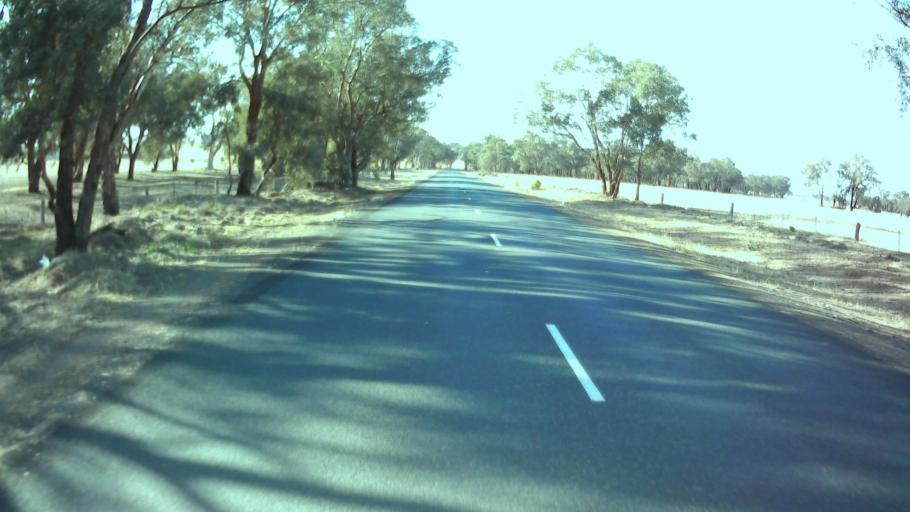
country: AU
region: New South Wales
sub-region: Weddin
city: Grenfell
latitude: -33.9466
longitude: 148.1364
